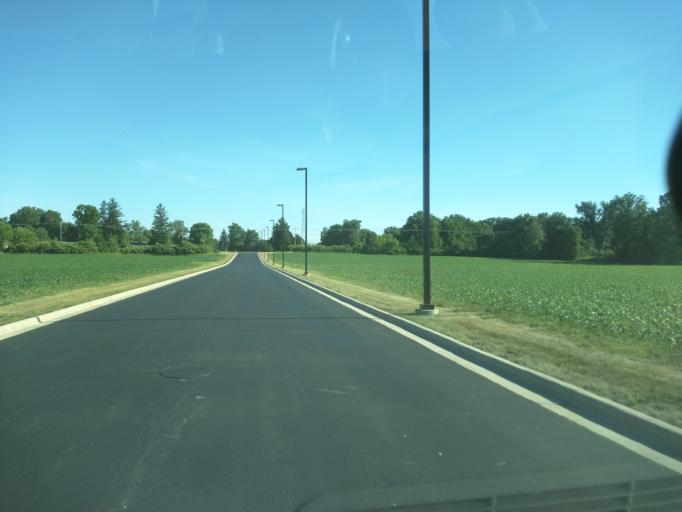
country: US
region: Michigan
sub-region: Eaton County
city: Waverly
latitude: 42.7145
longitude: -84.6359
